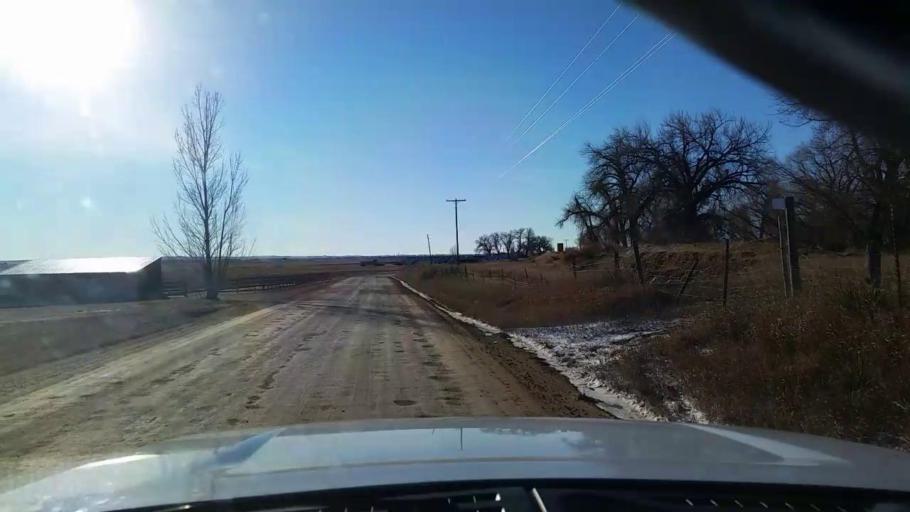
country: US
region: Colorado
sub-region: Larimer County
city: Wellington
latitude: 40.7595
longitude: -105.0375
